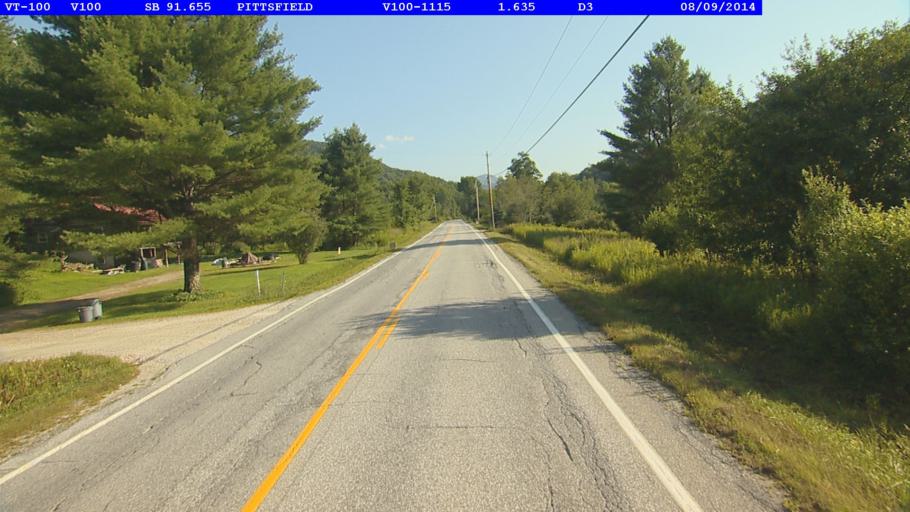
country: US
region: Vermont
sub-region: Rutland County
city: Rutland
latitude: 43.7406
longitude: -72.8202
